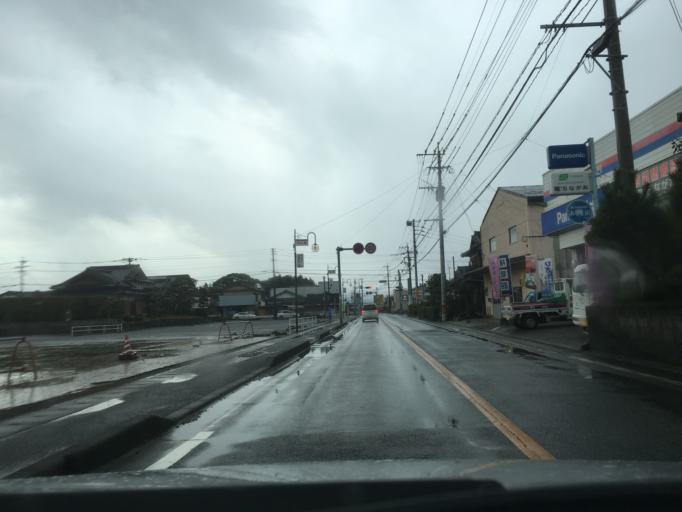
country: JP
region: Saga Prefecture
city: Tosu
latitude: 33.3778
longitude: 130.5610
